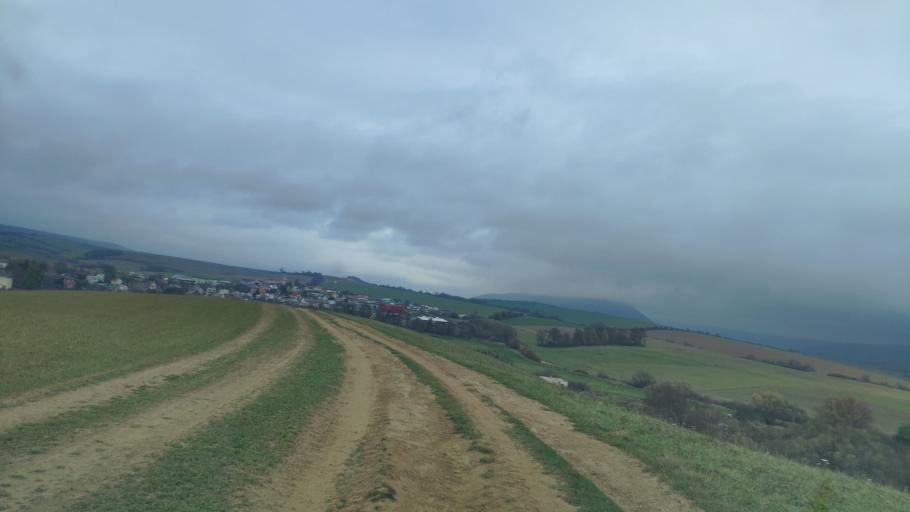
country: SK
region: Presovsky
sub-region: Okres Presov
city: Presov
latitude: 49.0091
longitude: 21.1941
